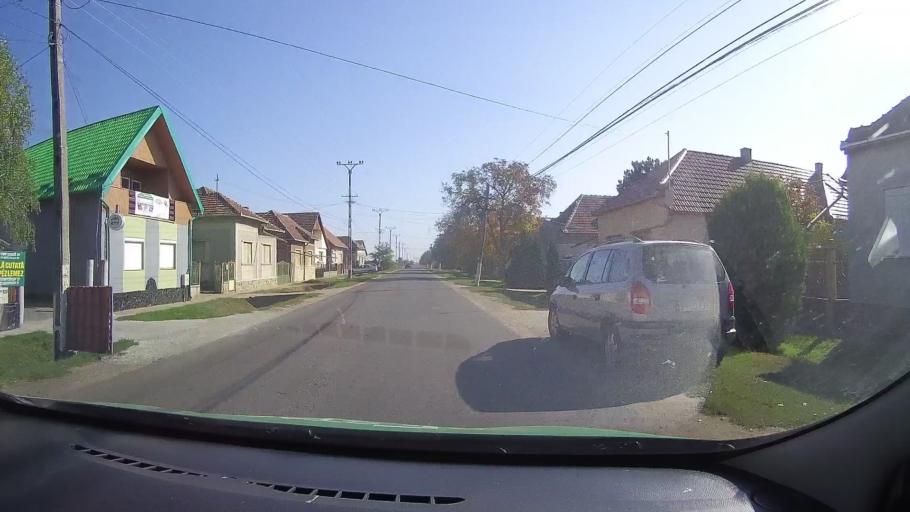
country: RO
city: Foieni
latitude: 47.6953
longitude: 22.3975
